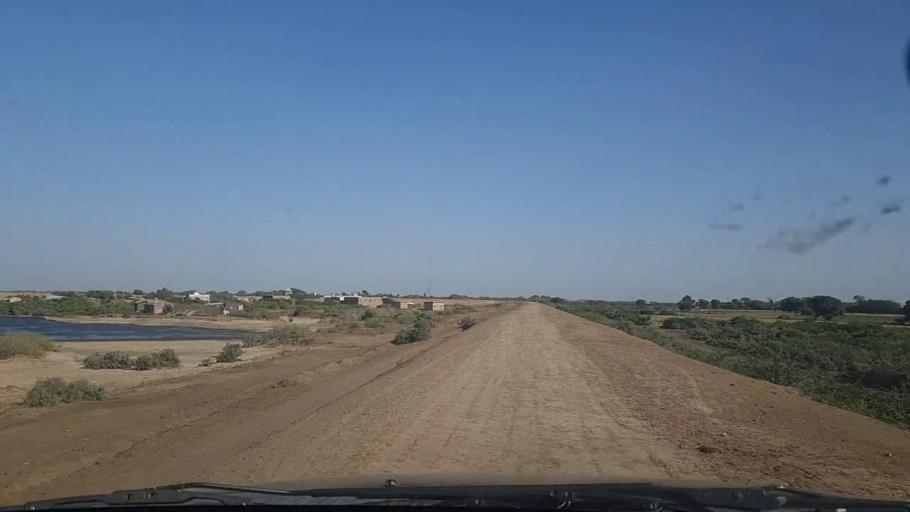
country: PK
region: Sindh
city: Chuhar Jamali
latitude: 24.3695
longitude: 67.7741
